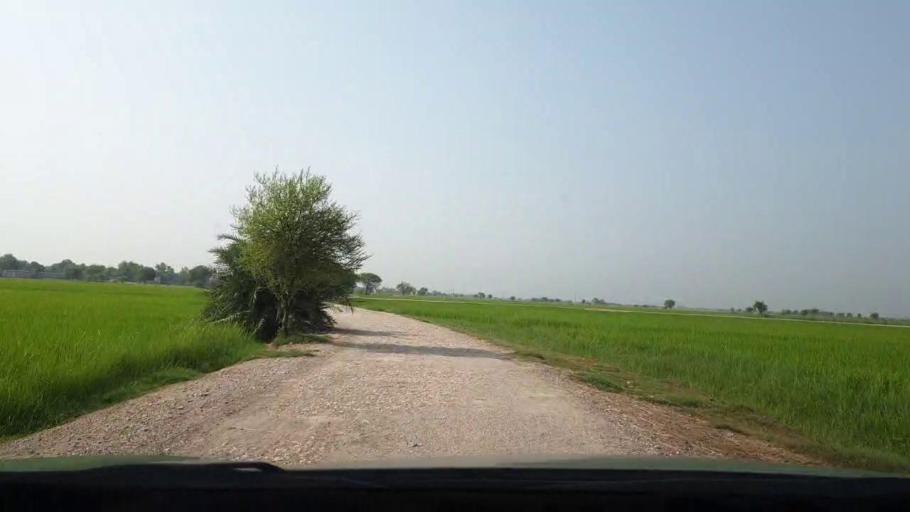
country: PK
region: Sindh
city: Goth Garelo
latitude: 27.4670
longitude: 68.0891
